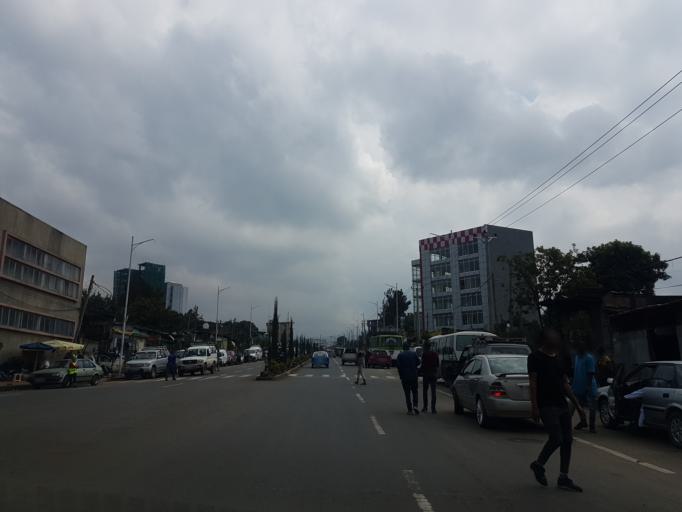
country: ET
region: Adis Abeba
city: Addis Ababa
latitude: 9.0191
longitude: 38.7353
